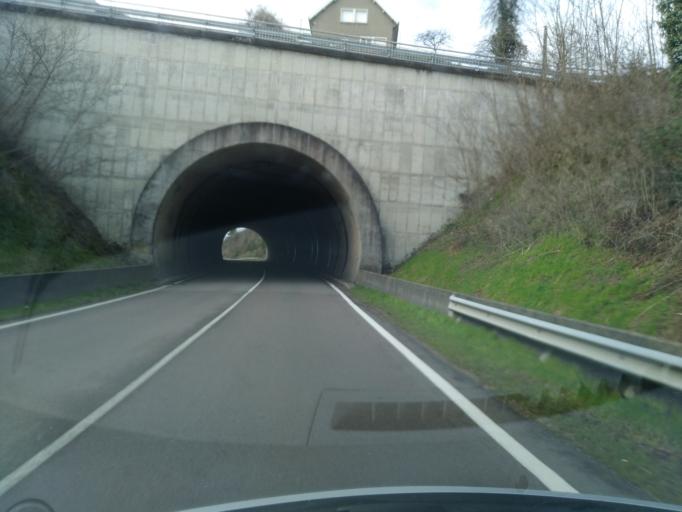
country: FR
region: Bourgogne
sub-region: Departement de Saone-et-Loire
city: Montcenis
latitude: 46.7977
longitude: 4.3915
